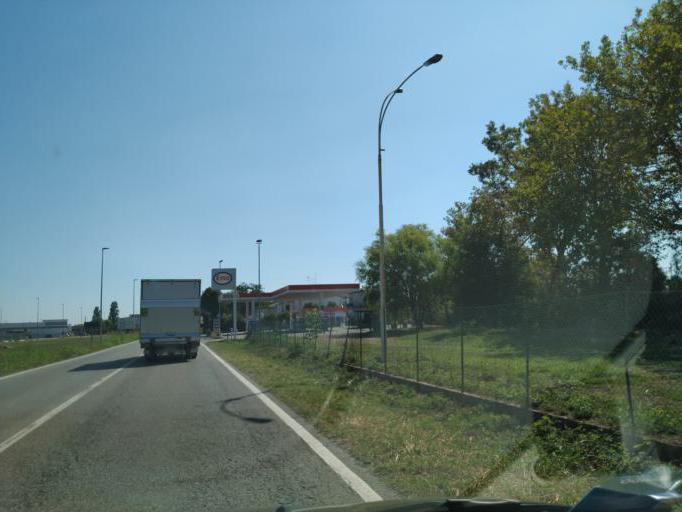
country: IT
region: Emilia-Romagna
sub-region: Provincia di Ferrara
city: Copparo
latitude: 44.8896
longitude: 11.8010
